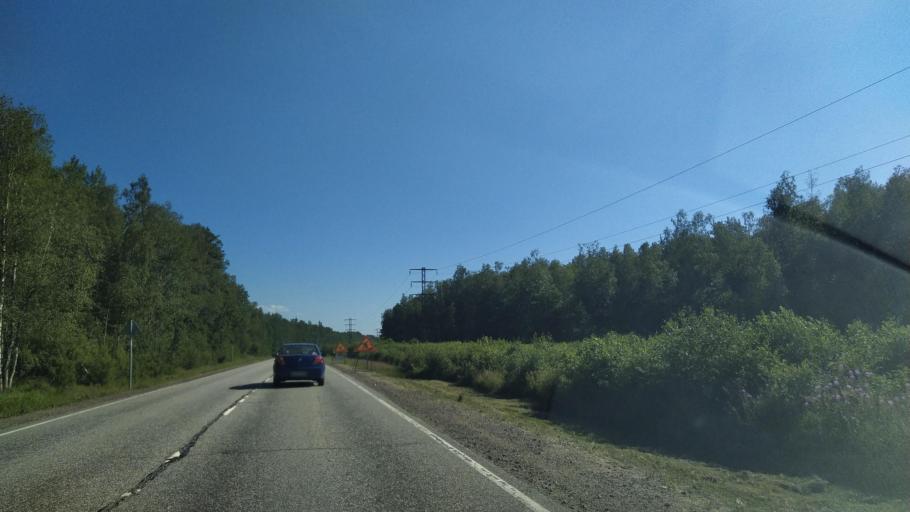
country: RU
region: Leningrad
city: Imeni Morozova
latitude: 60.0457
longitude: 31.0349
